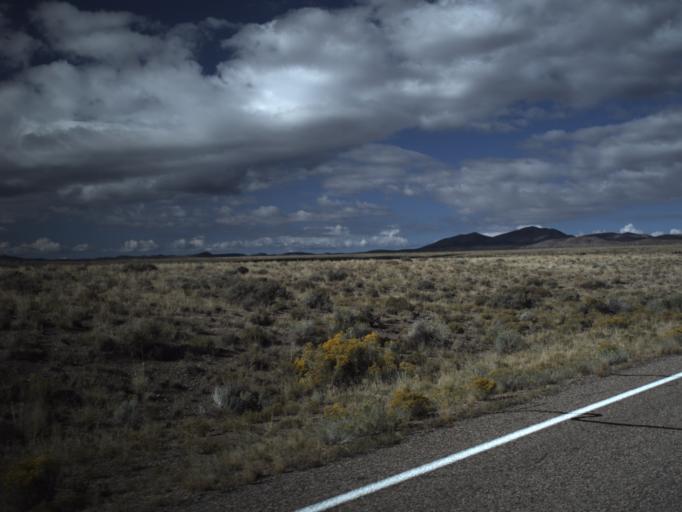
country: US
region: Utah
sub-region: Beaver County
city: Milford
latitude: 38.4405
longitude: -113.1615
